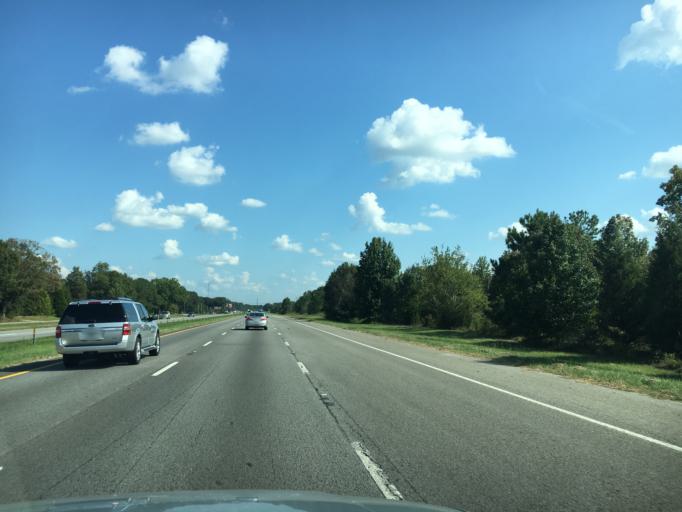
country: US
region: South Carolina
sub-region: Greenville County
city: Fountain Inn
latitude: 34.6617
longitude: -82.1731
